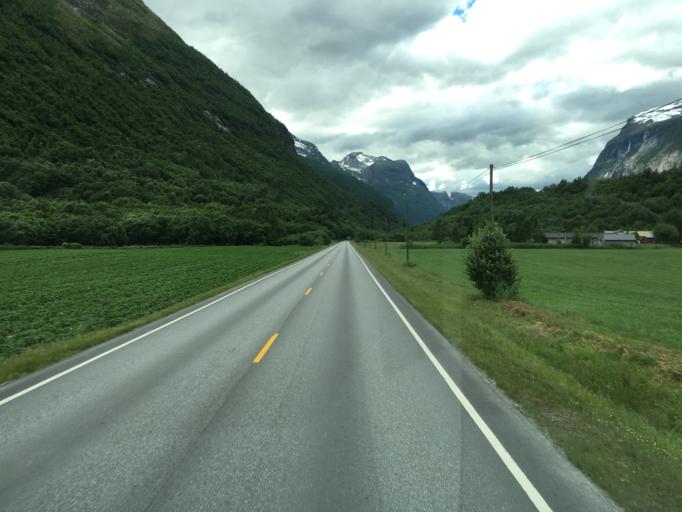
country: NO
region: More og Romsdal
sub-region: Sunndal
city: Sunndalsora
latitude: 62.6408
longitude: 8.7754
